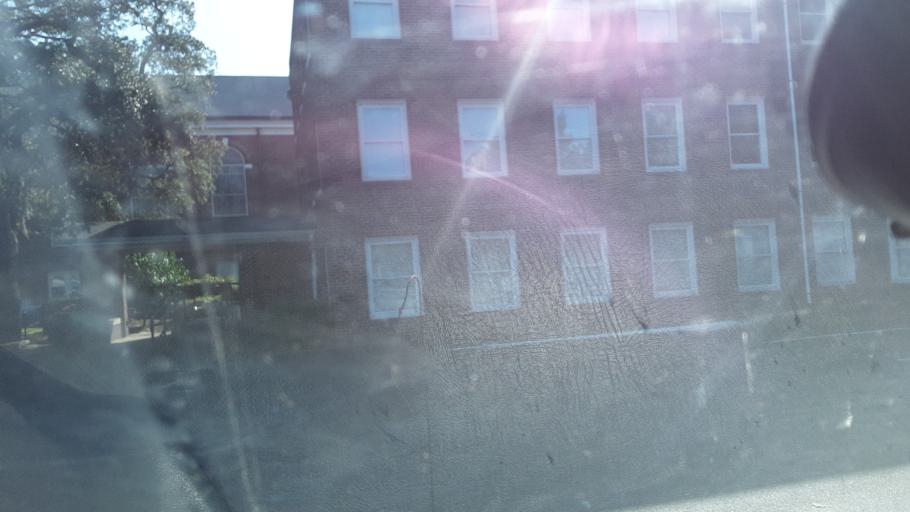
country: US
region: South Carolina
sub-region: Horry County
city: Myrtle Beach
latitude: 33.6896
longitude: -78.8876
